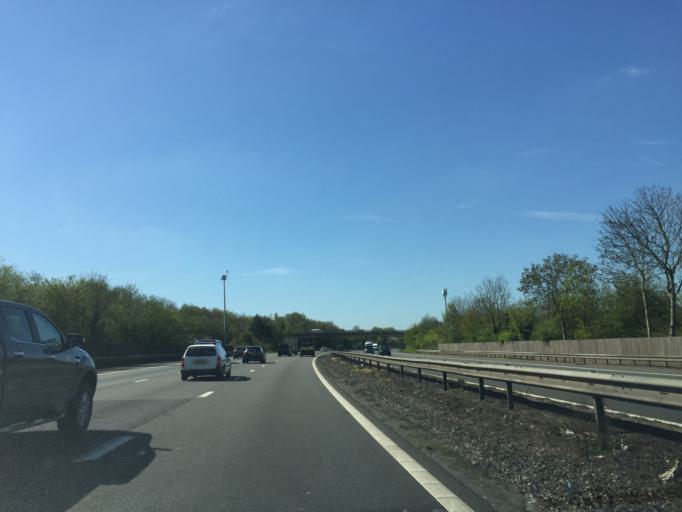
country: GB
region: England
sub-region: Essex
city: Chigwell
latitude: 51.6187
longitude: 0.0628
